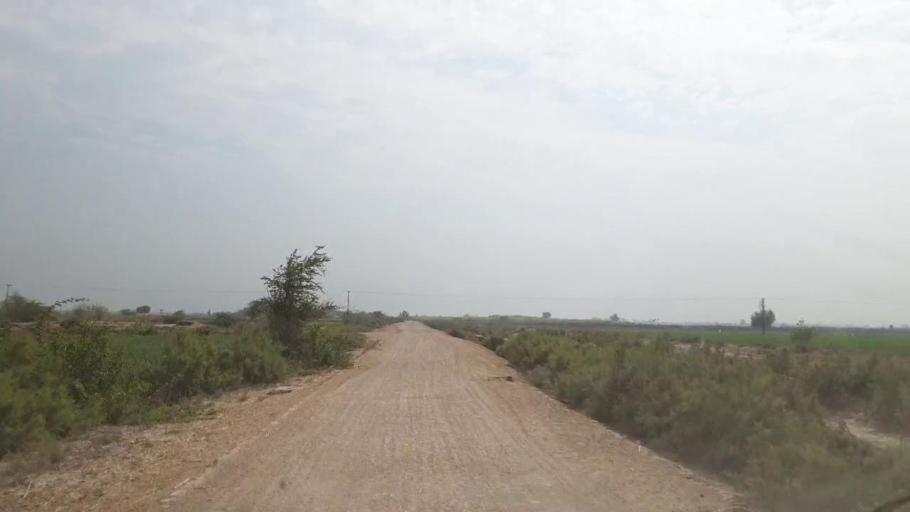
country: PK
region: Sindh
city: Mirpur Khas
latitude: 25.5426
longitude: 69.1270
